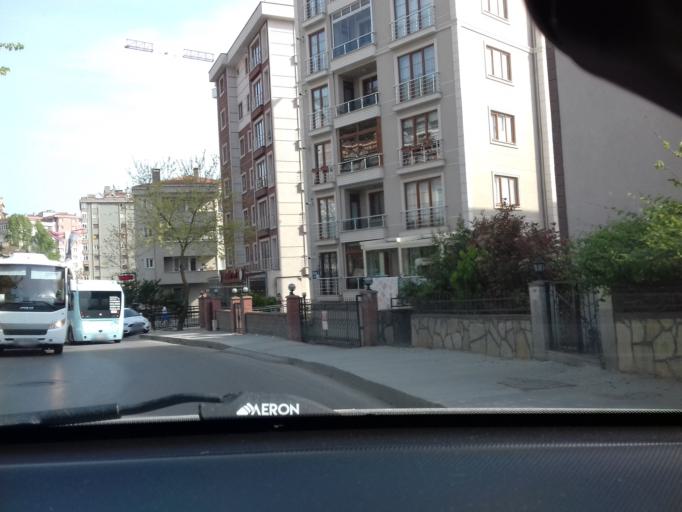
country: TR
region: Istanbul
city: Pendik
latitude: 40.9103
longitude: 29.2338
